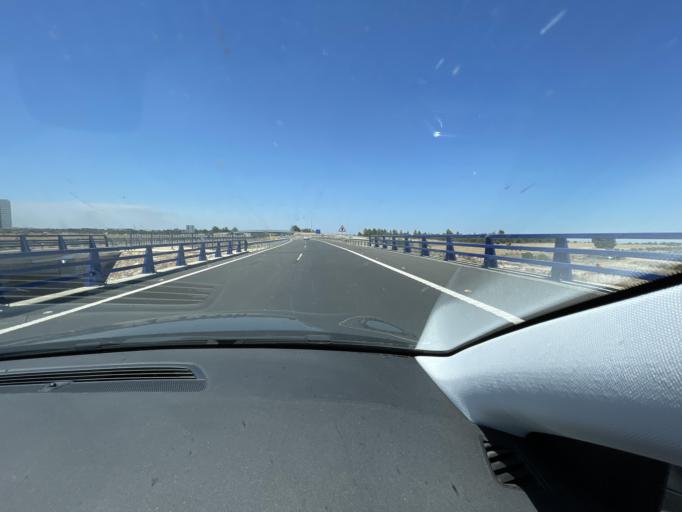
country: ES
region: Castille and Leon
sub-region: Provincia de Salamanca
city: Fuentes de Onoro
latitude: 40.6126
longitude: -6.8183
